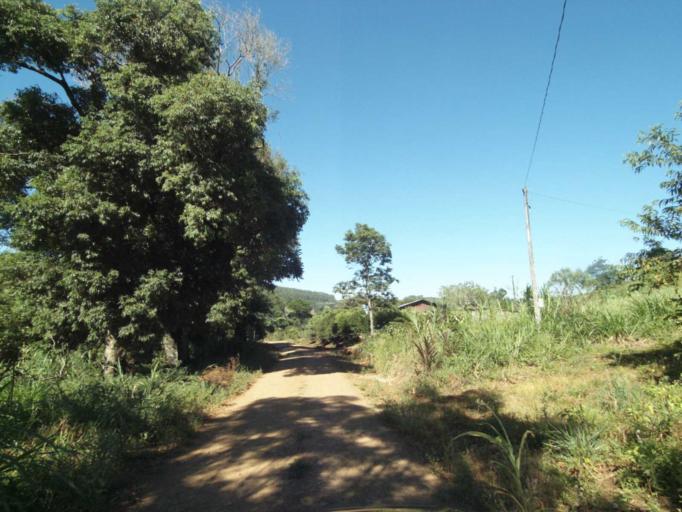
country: BR
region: Parana
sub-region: Francisco Beltrao
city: Francisco Beltrao
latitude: -26.1413
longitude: -53.3108
